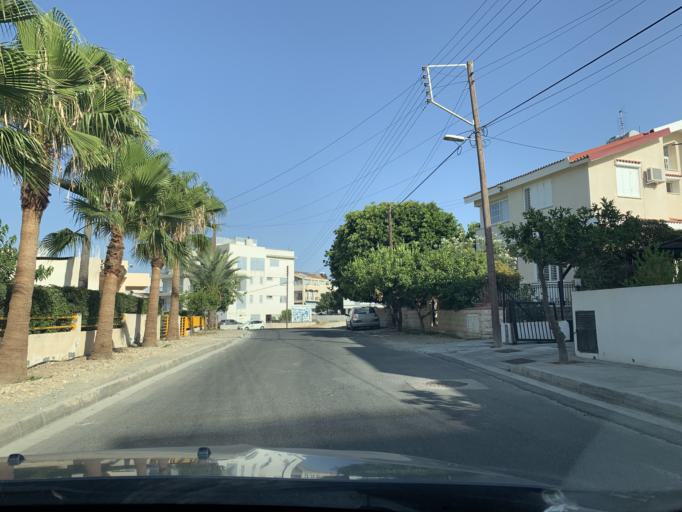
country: CY
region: Lefkosia
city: Nicosia
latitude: 35.1514
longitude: 33.3922
